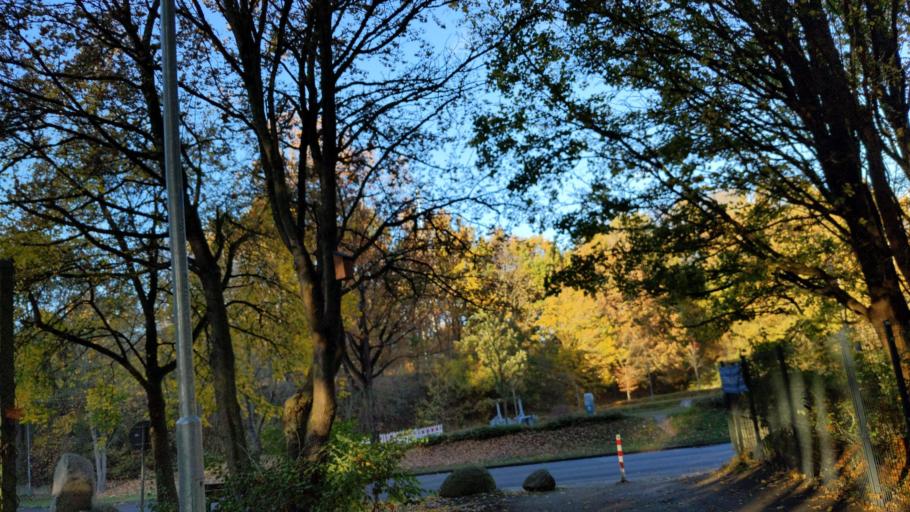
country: DE
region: Schleswig-Holstein
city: Sierksdorf
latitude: 54.0713
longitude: 10.7785
